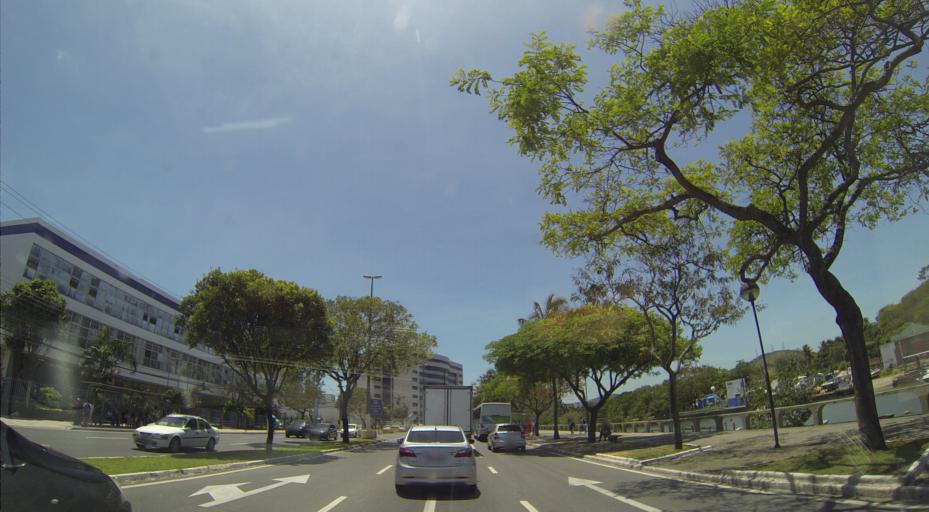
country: BR
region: Espirito Santo
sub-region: Vitoria
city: Vitoria
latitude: -20.3170
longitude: -40.3143
